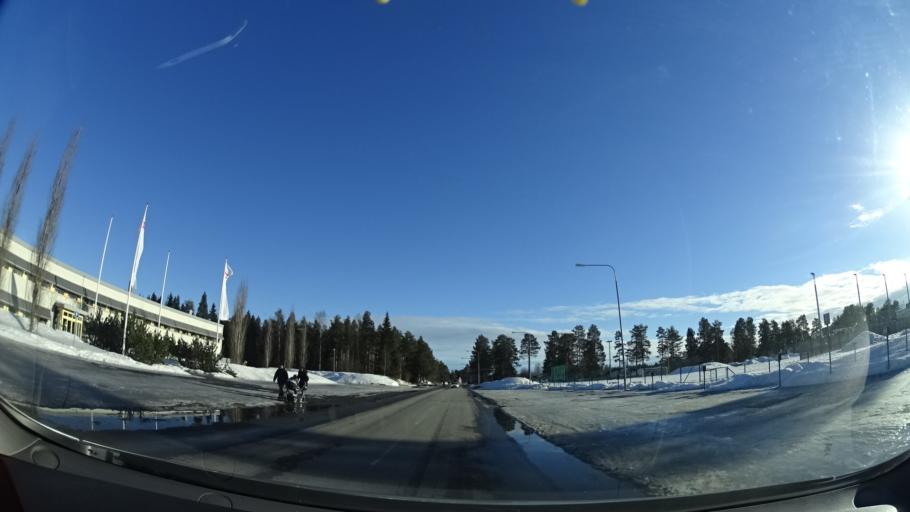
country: SE
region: Vaesterbotten
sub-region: Skelleftea Kommun
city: Byske
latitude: 64.9557
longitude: 21.2107
